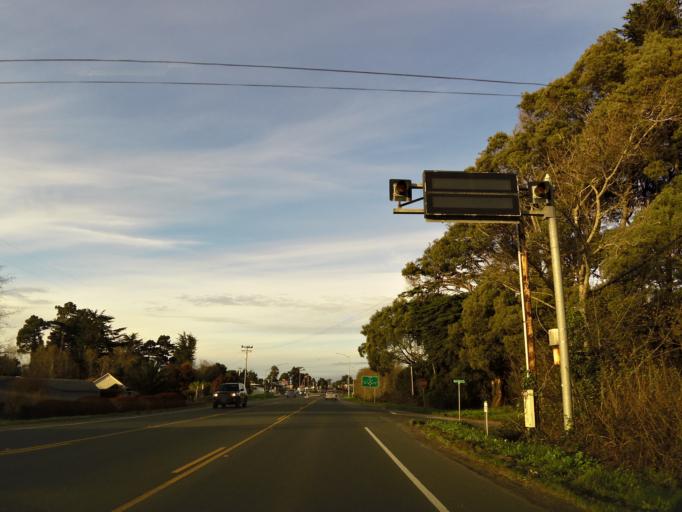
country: US
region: California
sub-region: Mendocino County
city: Fort Bragg
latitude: 39.4104
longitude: -123.8085
